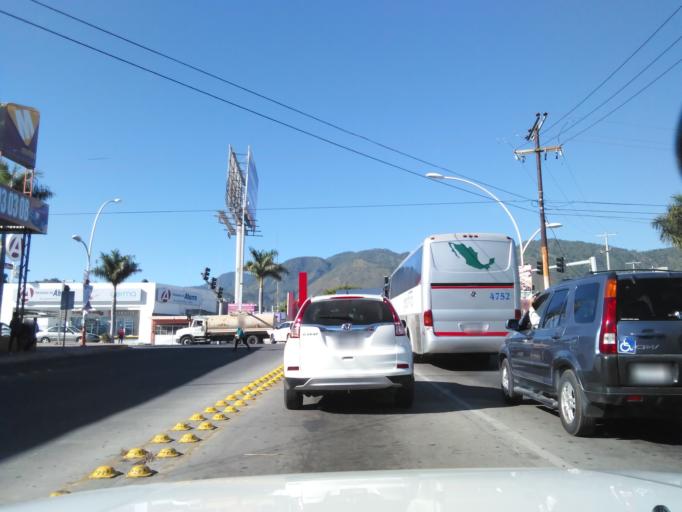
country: MX
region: Nayarit
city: Tepic
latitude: 21.4889
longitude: -104.8942
